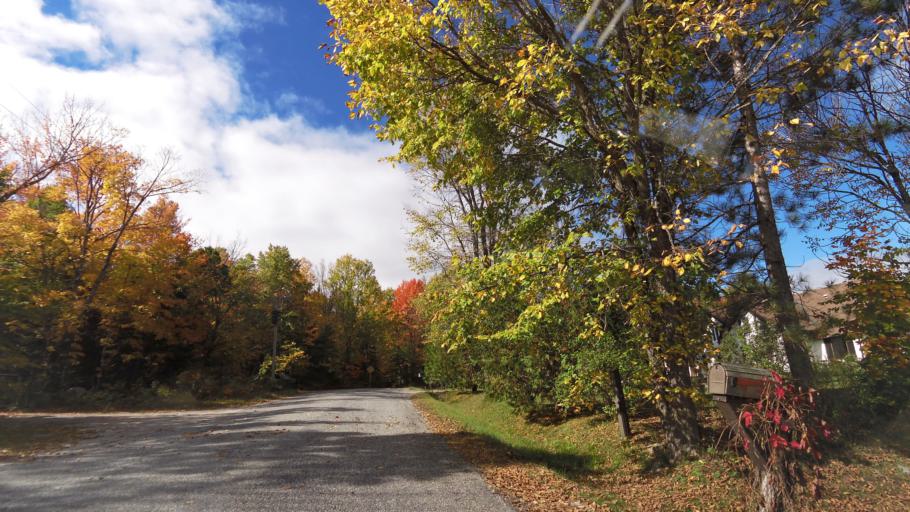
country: CA
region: Ontario
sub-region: Nipissing District
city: North Bay
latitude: 46.3760
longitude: -79.4923
